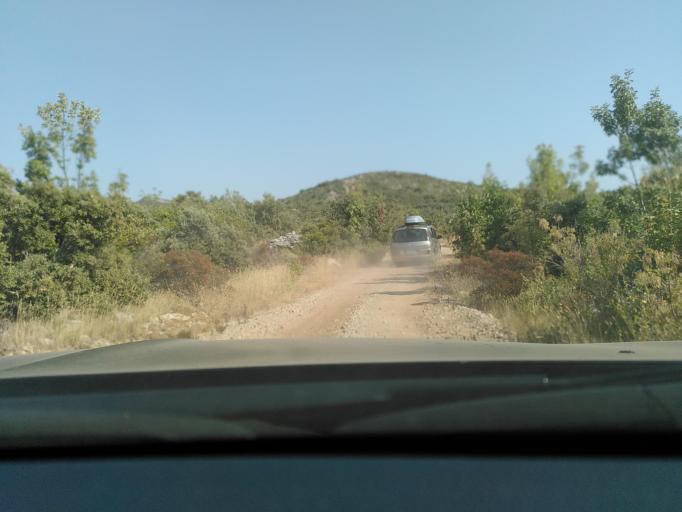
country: HR
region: Splitsko-Dalmatinska
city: Stari Grad
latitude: 43.1617
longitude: 16.5541
